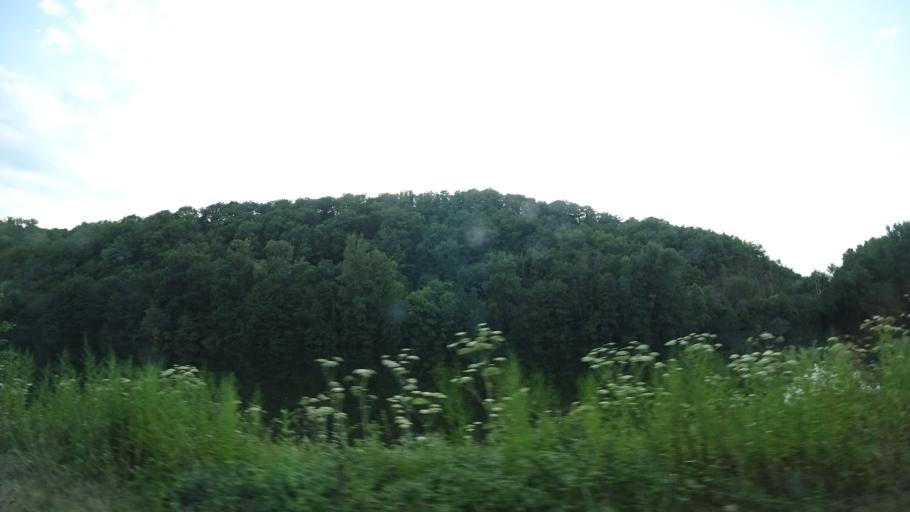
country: FR
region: Midi-Pyrenees
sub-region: Departement de l'Aveyron
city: Livinhac-le-Haut
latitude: 44.6069
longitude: 2.2328
